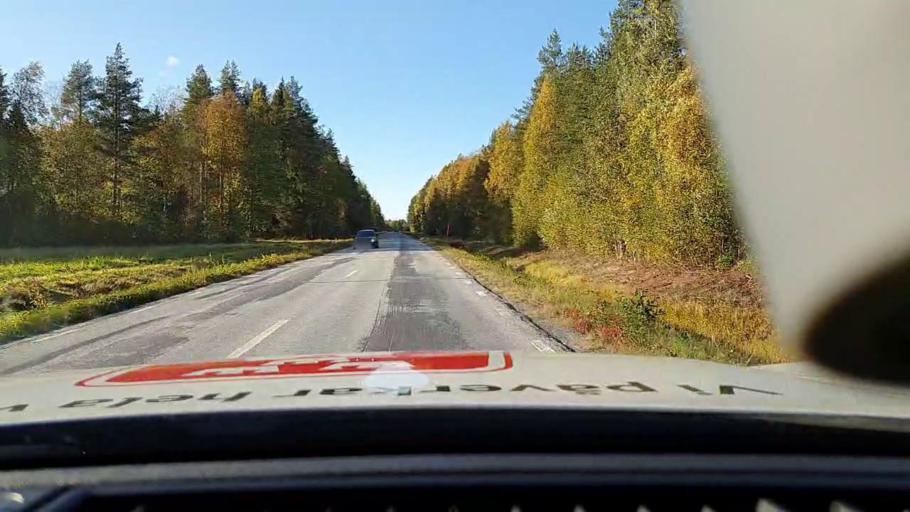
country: SE
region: Norrbotten
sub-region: Pitea Kommun
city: Norrfjarden
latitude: 65.4349
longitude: 21.4817
